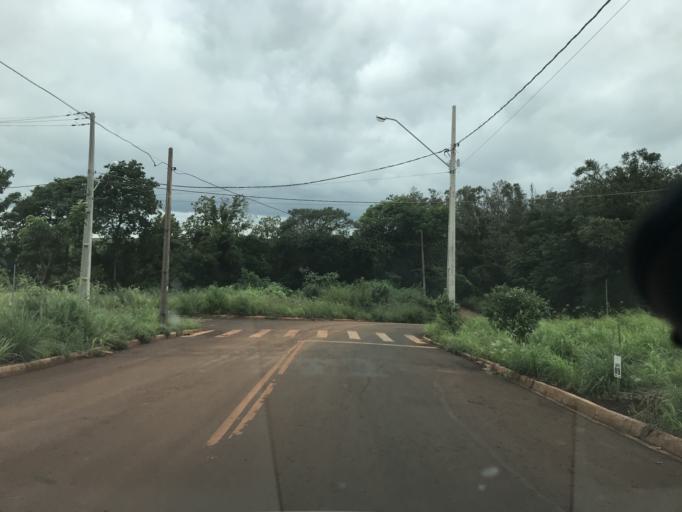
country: BR
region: Parana
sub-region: Palotina
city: Palotina
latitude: -24.2914
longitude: -53.8239
